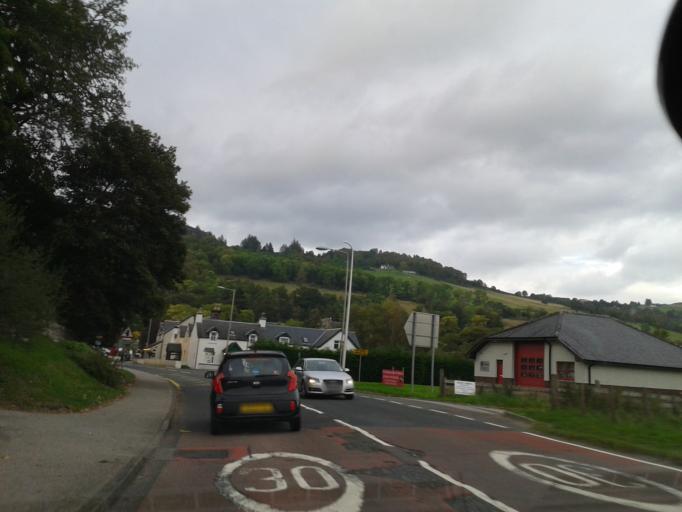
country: GB
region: Scotland
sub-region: Highland
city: Beauly
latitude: 57.3343
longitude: -4.4799
